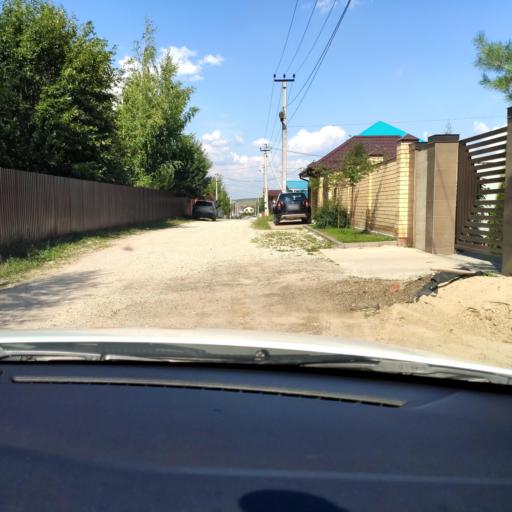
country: RU
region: Tatarstan
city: Stolbishchi
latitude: 55.7344
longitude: 49.2614
